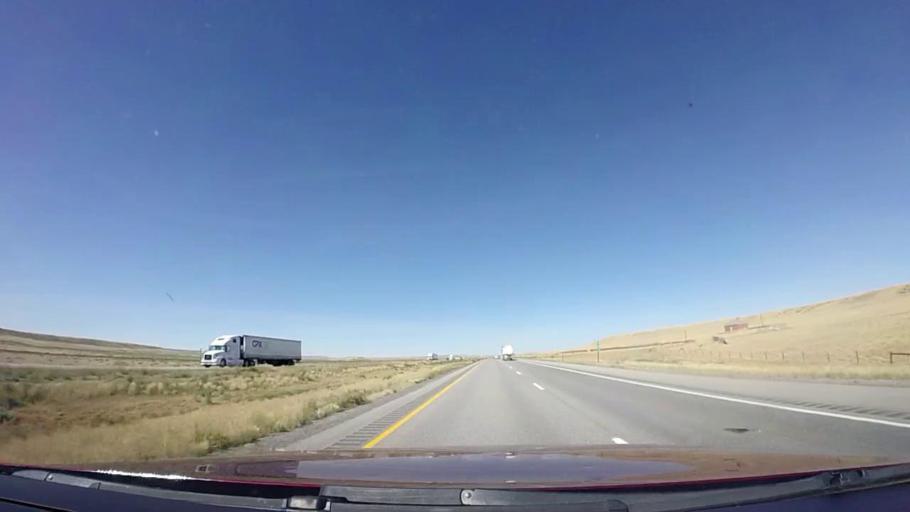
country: US
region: Wyoming
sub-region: Carbon County
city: Rawlins
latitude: 41.6562
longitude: -108.1014
